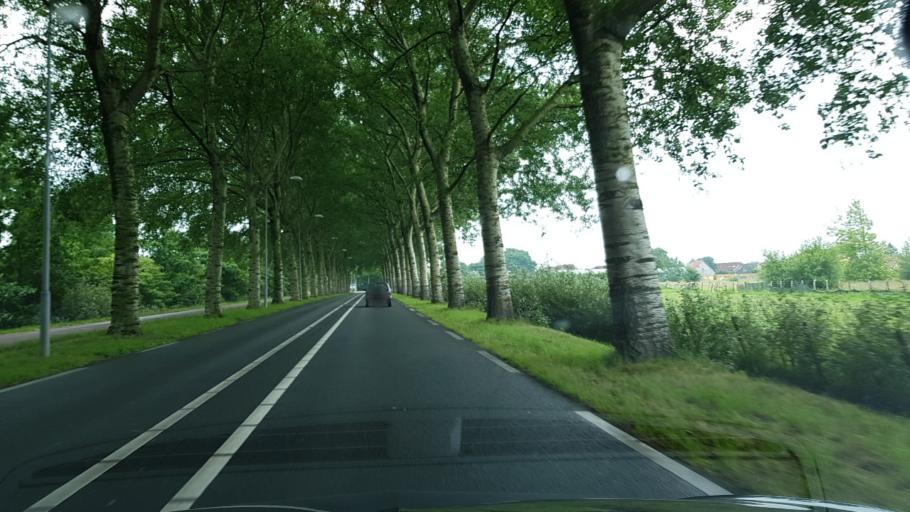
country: NL
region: North Holland
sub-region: Gemeente Velsen
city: Velsen-Zuid
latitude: 52.4442
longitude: 4.6568
